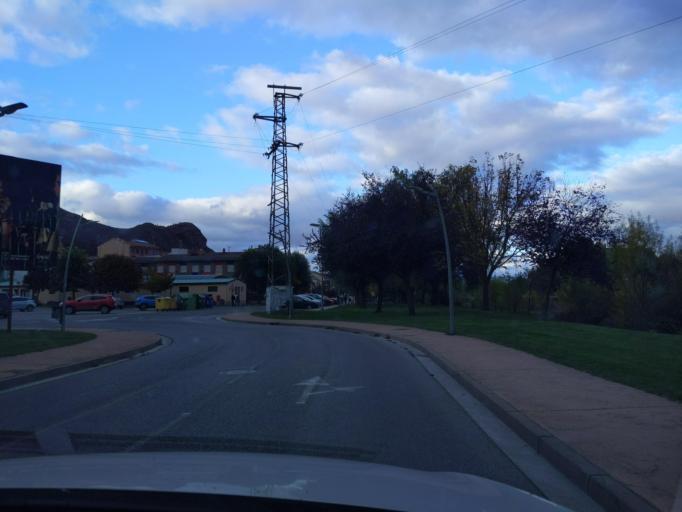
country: ES
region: La Rioja
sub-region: Provincia de La Rioja
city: Najera
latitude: 42.4143
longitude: -2.7338
